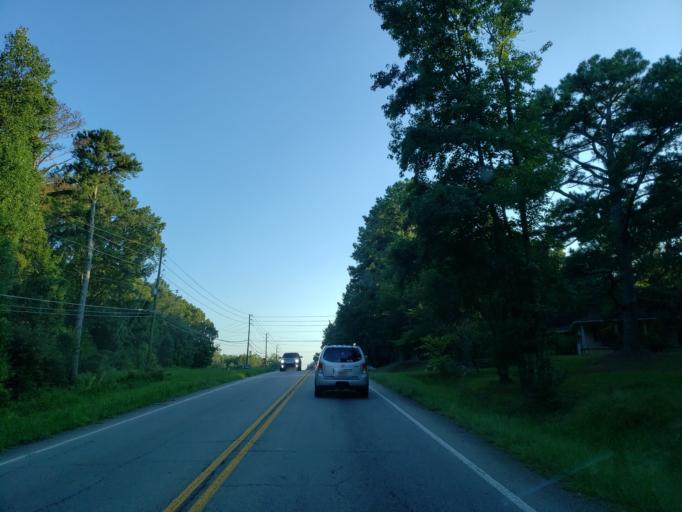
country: US
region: Georgia
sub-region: Paulding County
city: Dallas
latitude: 33.9826
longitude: -84.7737
